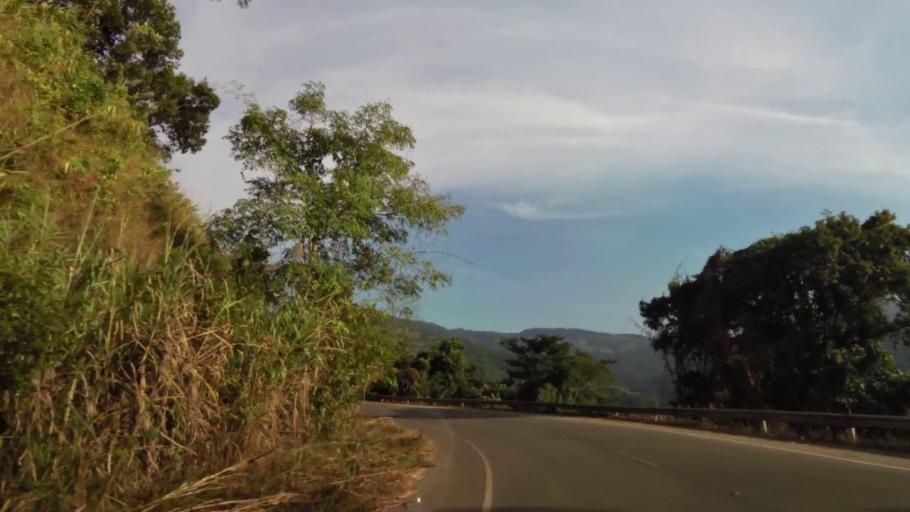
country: TH
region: Chiang Rai
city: Khun Tan
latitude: 19.8673
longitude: 100.4071
